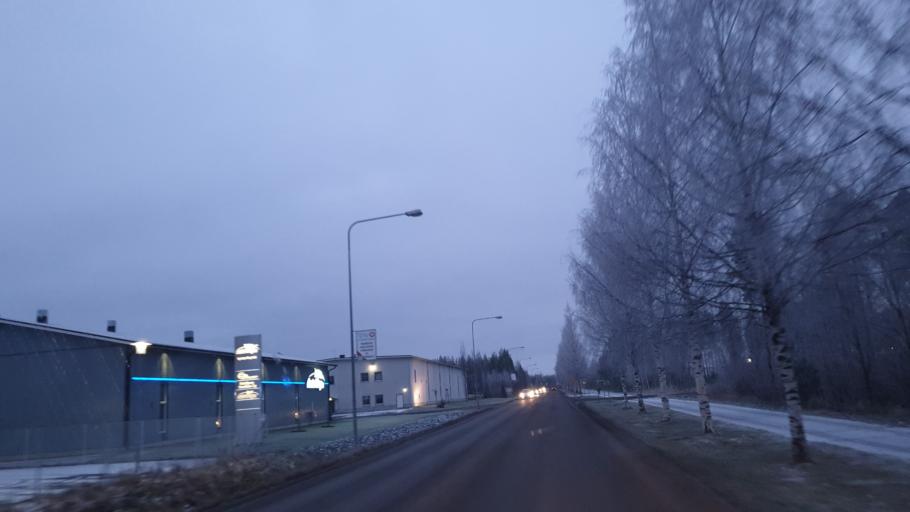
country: FI
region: Southern Ostrobothnia
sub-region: Seinaejoki
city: Nurmo
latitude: 62.7833
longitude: 22.9000
